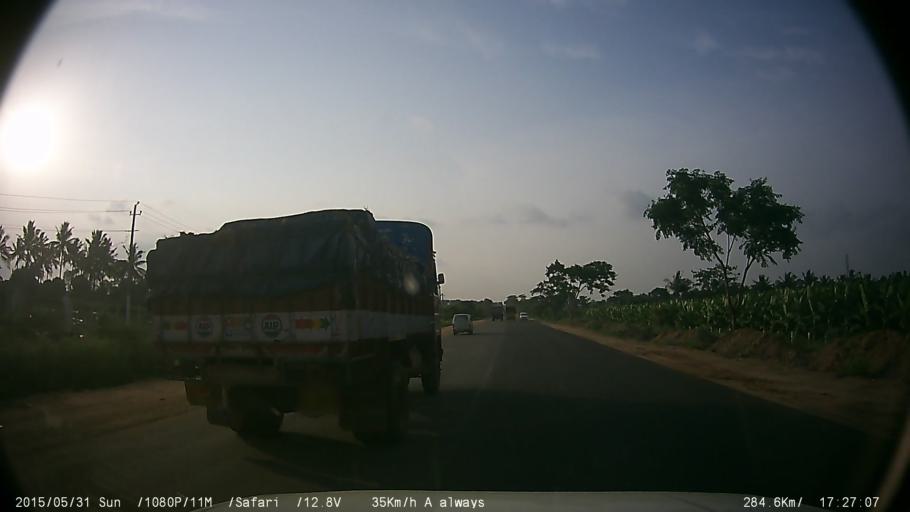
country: IN
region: Karnataka
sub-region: Chamrajnagar
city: Gundlupet
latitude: 11.8578
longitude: 76.6701
